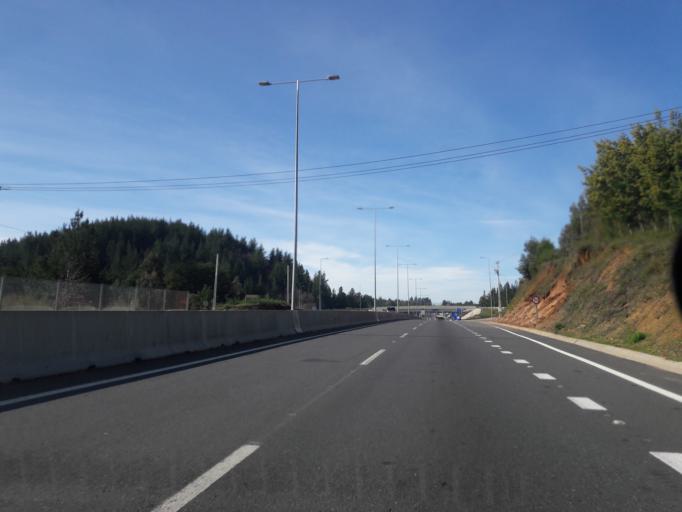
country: CL
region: Biobio
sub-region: Provincia de Biobio
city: Yumbel
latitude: -36.9594
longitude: -72.7350
